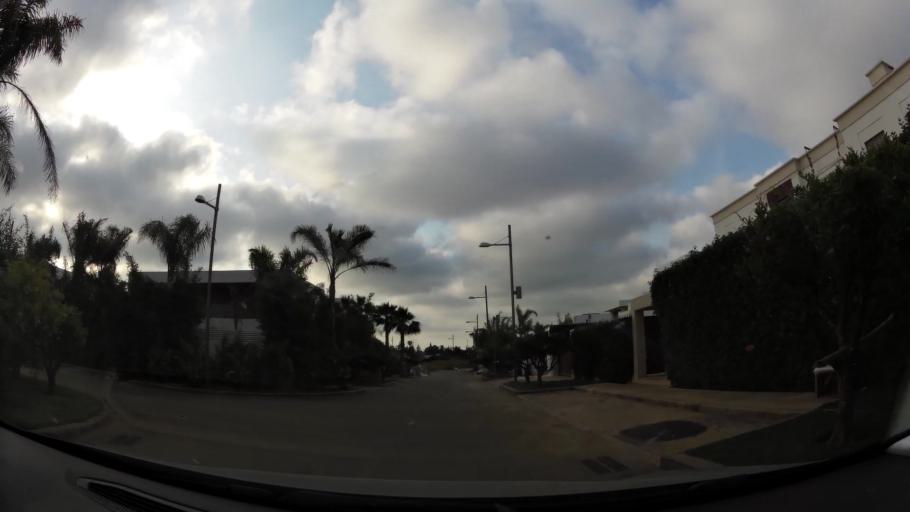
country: MA
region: Rabat-Sale-Zemmour-Zaer
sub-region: Rabat
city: Rabat
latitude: 33.9539
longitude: -6.8368
